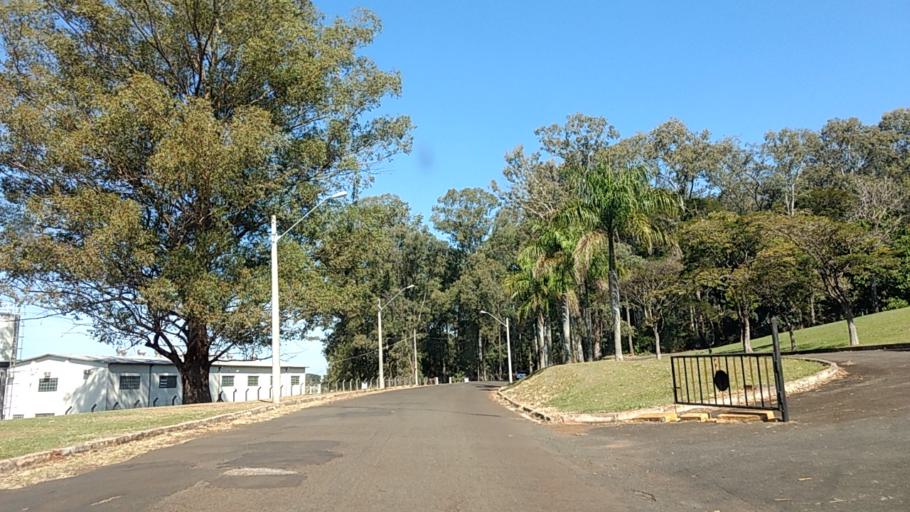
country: BR
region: Sao Paulo
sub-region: Botucatu
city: Botucatu
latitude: -22.8522
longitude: -48.4313
